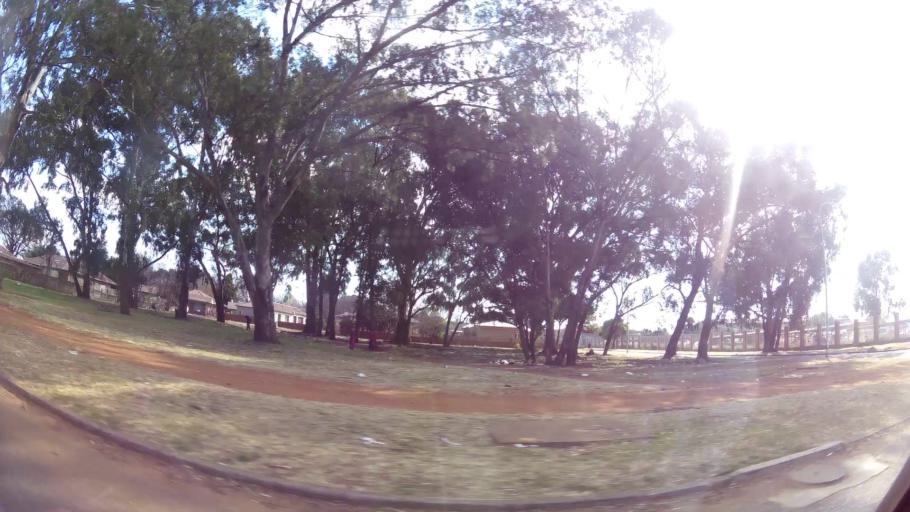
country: ZA
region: Gauteng
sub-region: Ekurhuleni Metropolitan Municipality
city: Germiston
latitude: -26.1924
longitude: 28.1634
